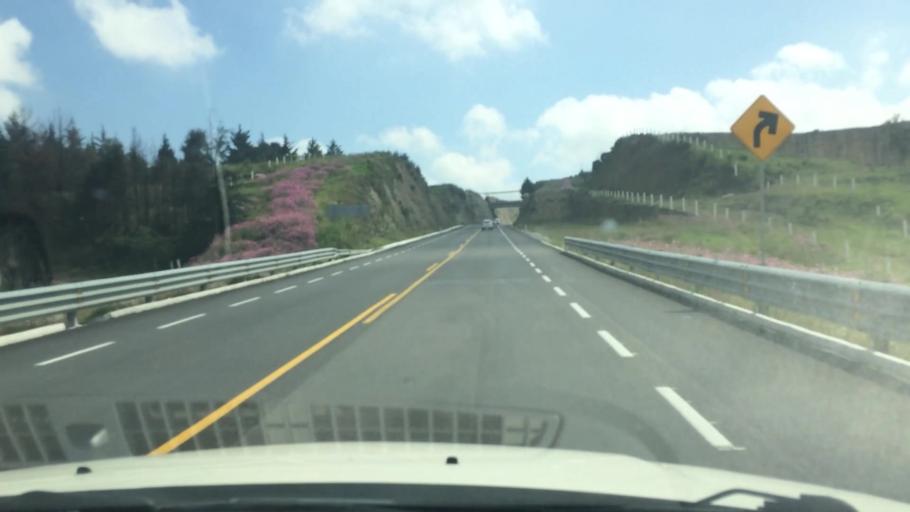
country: MX
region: Mexico
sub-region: Almoloya de Juarez
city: San Pedro de la Hortaliza (Ejido Almoloyan)
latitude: 19.3779
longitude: -99.8640
